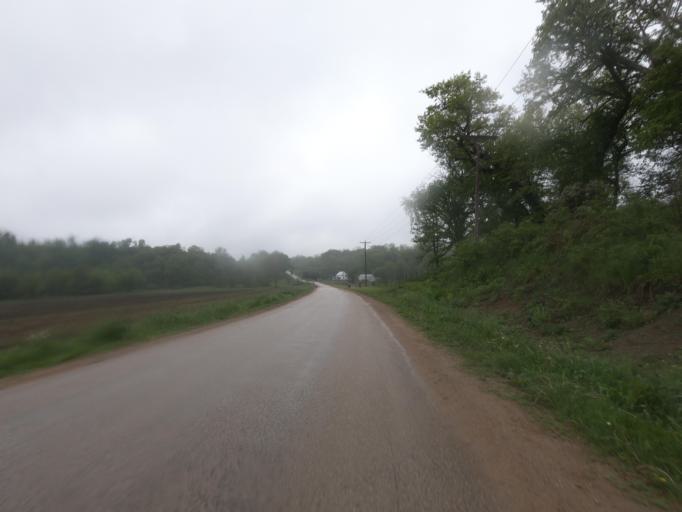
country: US
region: Wisconsin
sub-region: Grant County
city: Hazel Green
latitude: 42.5095
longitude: -90.4853
